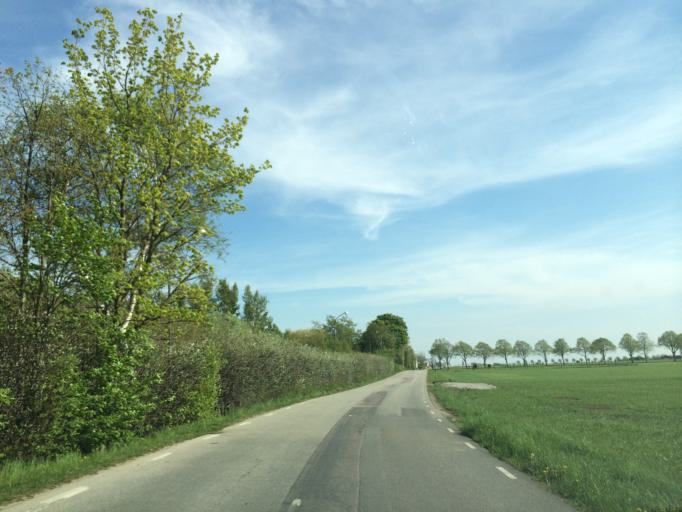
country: SE
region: Skane
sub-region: Kavlinge Kommun
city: Loddekopinge
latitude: 55.7420
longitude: 13.0596
